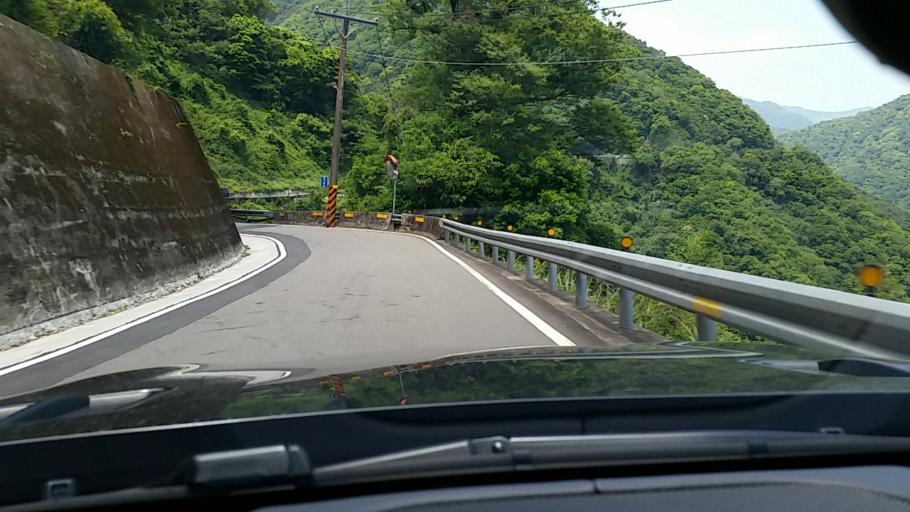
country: TW
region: Taiwan
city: Daxi
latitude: 24.6980
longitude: 121.3665
